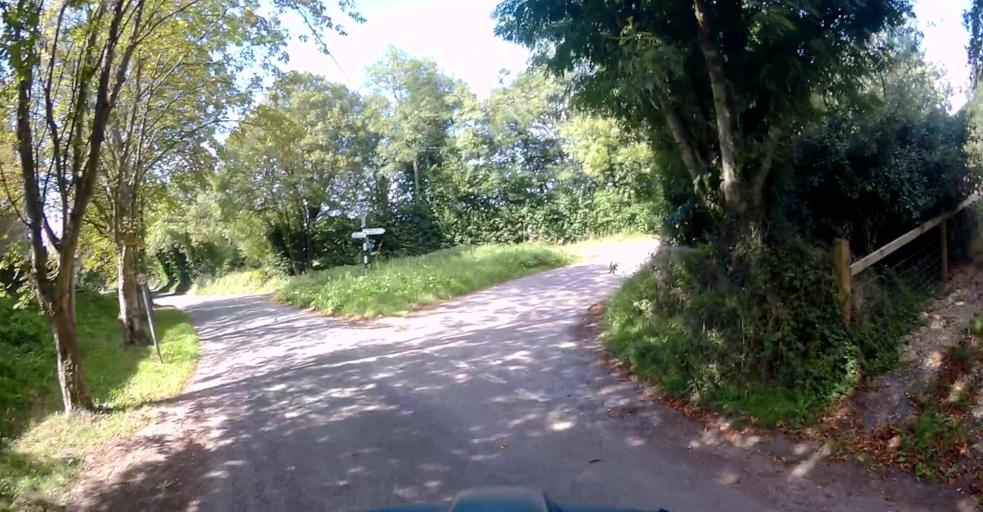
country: GB
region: England
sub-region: Hampshire
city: Four Marks
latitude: 51.1544
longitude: -1.0946
